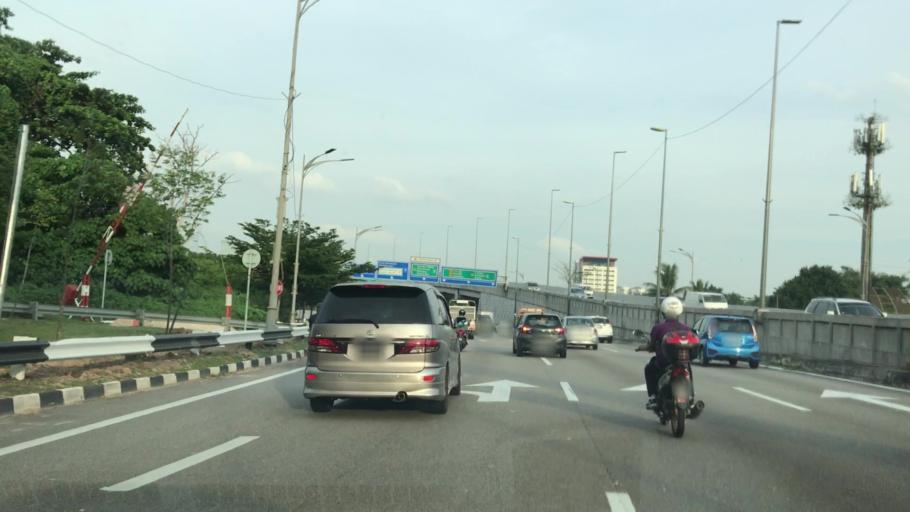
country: MY
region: Kuala Lumpur
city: Kuala Lumpur
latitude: 3.1236
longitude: 101.7040
